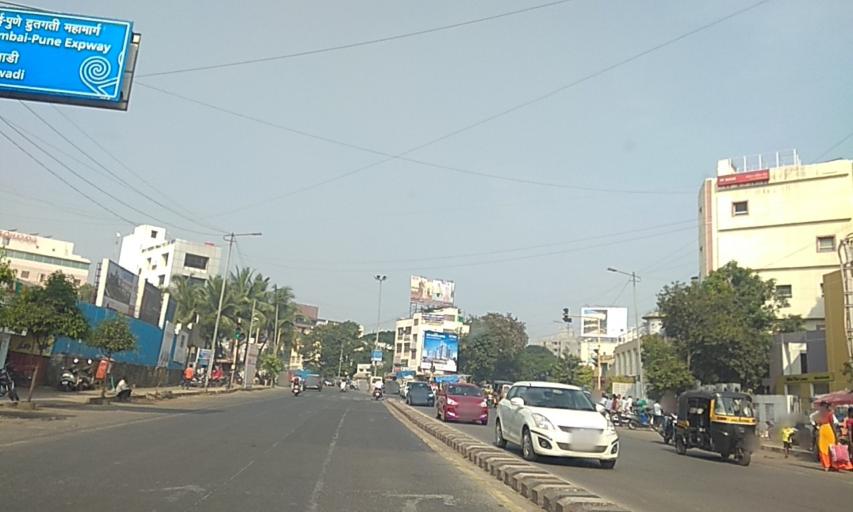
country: IN
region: Maharashtra
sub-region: Pune Division
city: Pimpri
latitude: 18.5631
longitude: 73.7833
